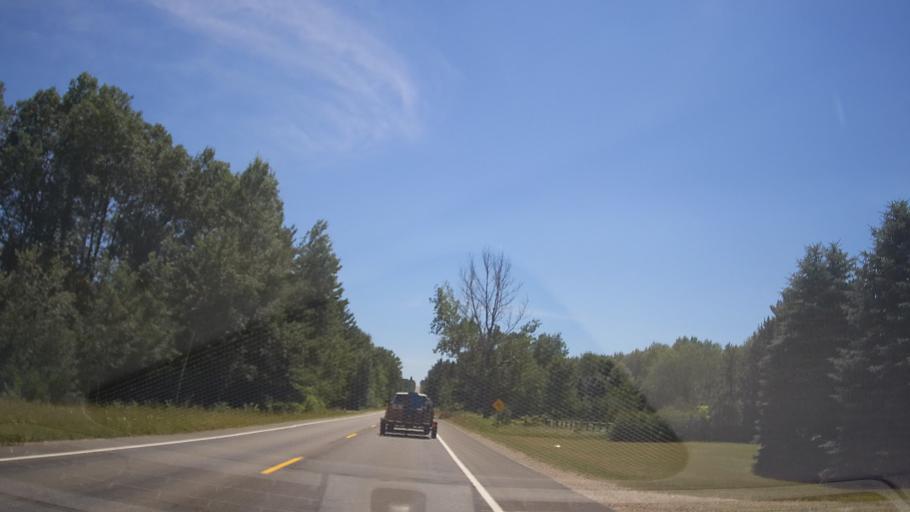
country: US
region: Michigan
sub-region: Grand Traverse County
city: Traverse City
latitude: 44.6372
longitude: -85.6964
